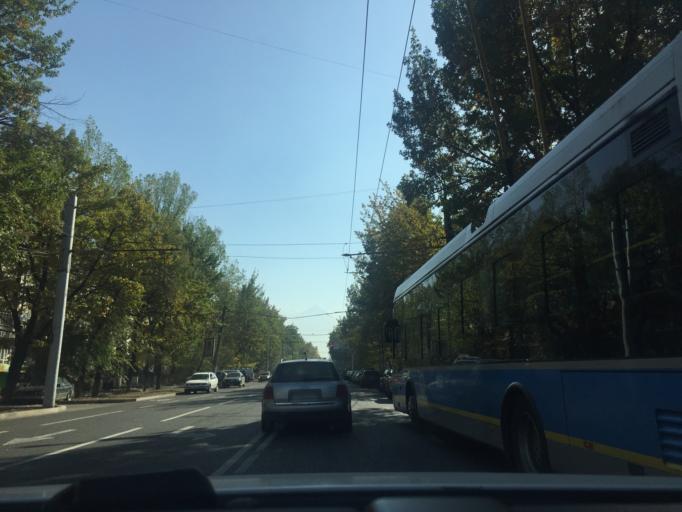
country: KZ
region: Almaty Qalasy
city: Almaty
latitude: 43.2517
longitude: 76.9024
